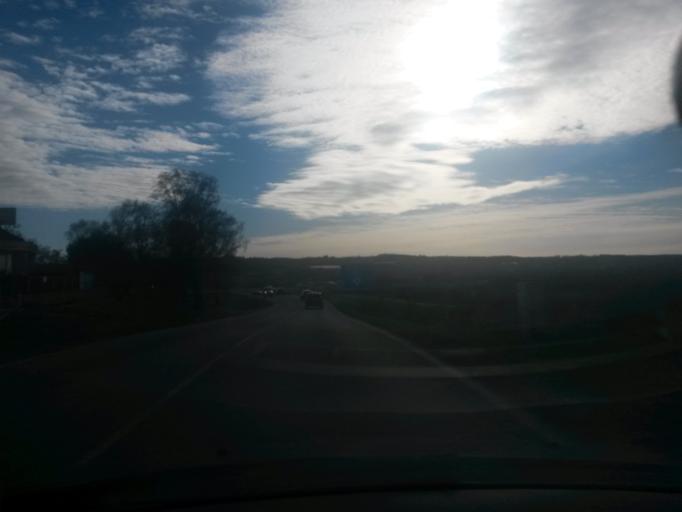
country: CZ
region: Central Bohemia
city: Jesenice
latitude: 49.9649
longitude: 14.5186
